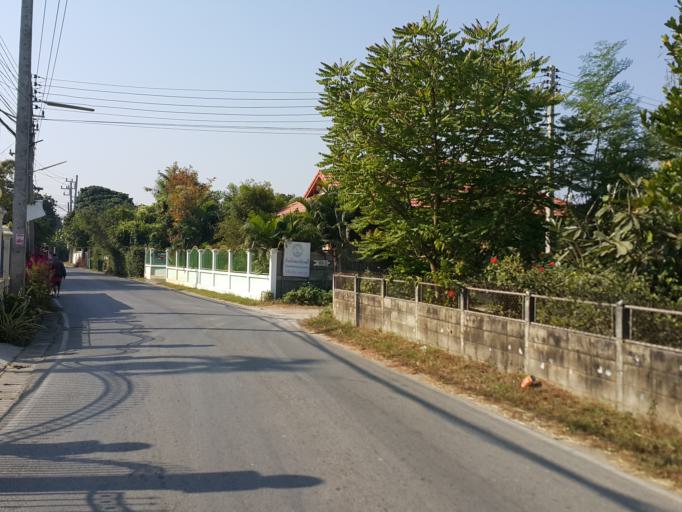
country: TH
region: Chiang Mai
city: San Kamphaeng
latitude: 18.7745
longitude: 99.0806
